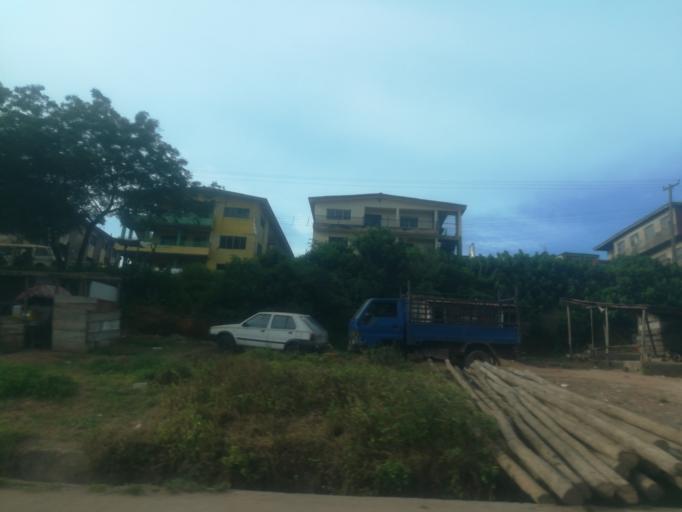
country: NG
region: Oyo
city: Ibadan
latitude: 7.3440
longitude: 3.9148
